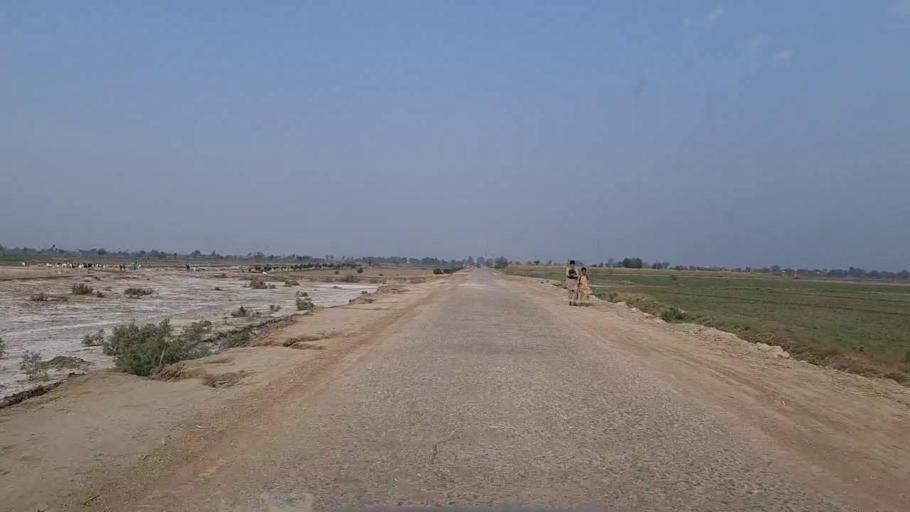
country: PK
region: Sindh
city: Mirwah Gorchani
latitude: 25.4172
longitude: 69.1466
